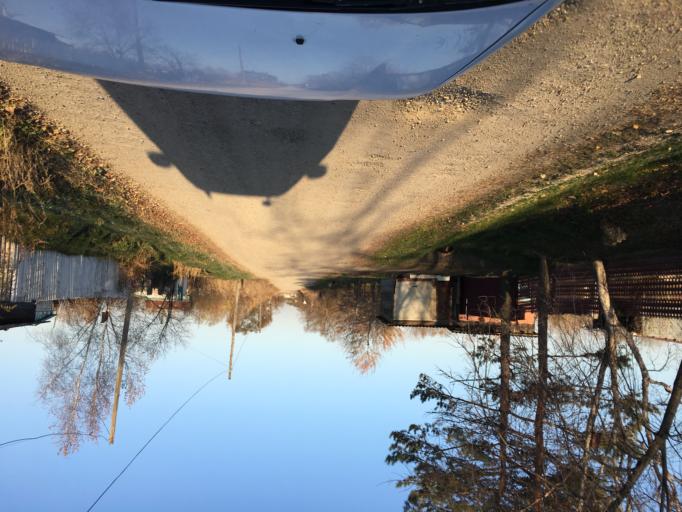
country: RU
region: Primorskiy
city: Lazo
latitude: 45.8634
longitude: 133.6438
